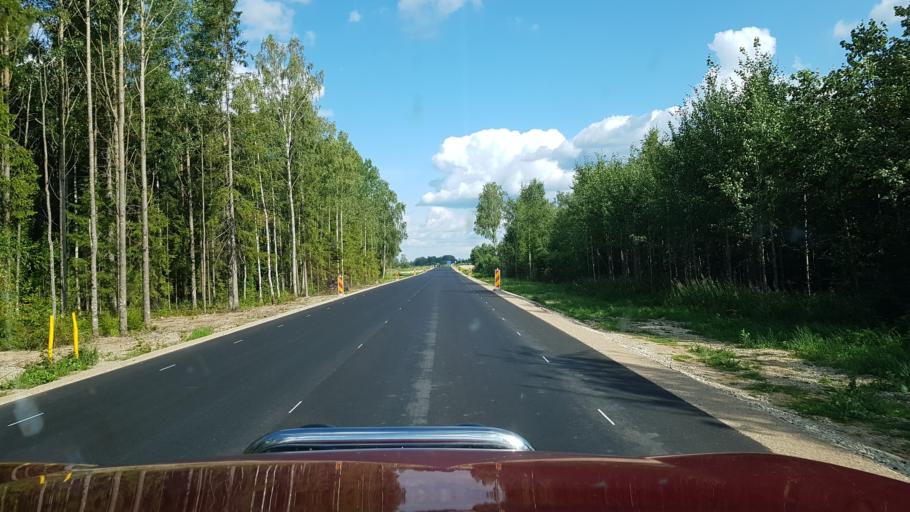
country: EE
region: Viljandimaa
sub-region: Moisakuela linn
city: Moisakula
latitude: 58.1184
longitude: 25.1857
